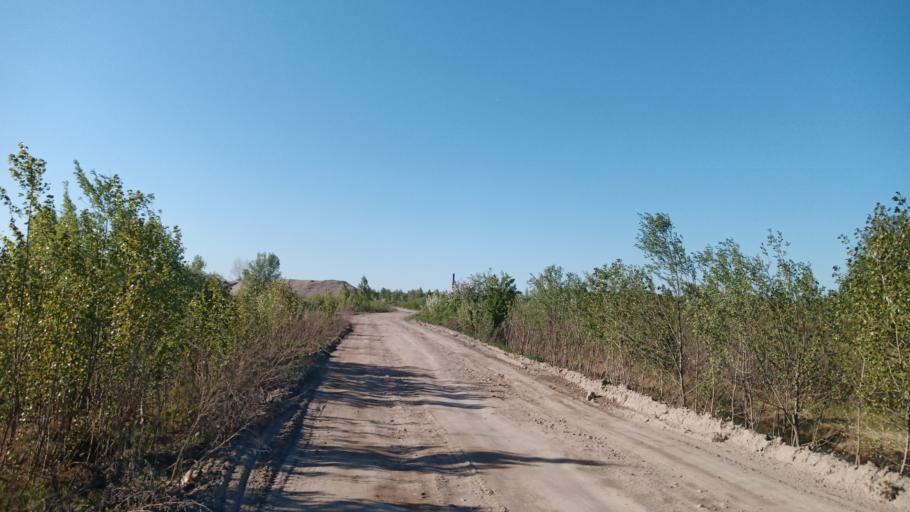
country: RU
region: Altai Krai
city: Zaton
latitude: 53.3074
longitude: 83.8242
